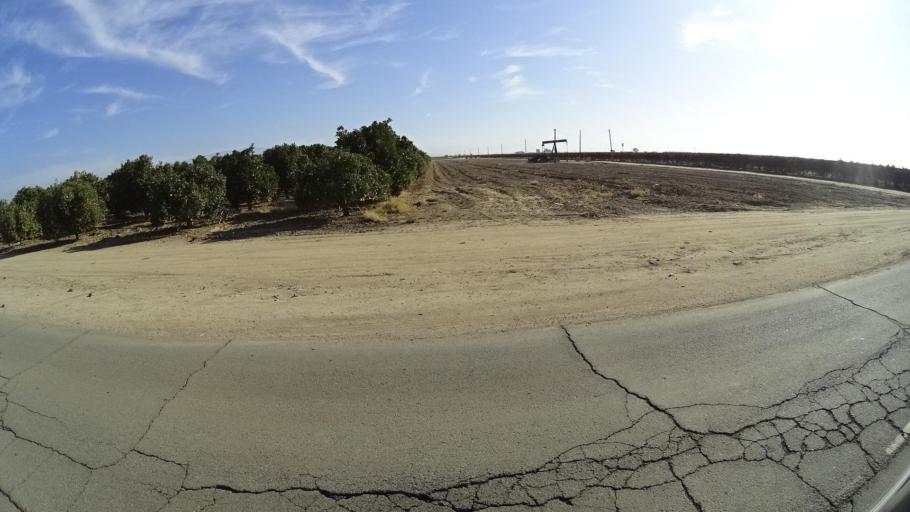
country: US
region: California
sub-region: Kern County
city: Lamont
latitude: 35.3427
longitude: -118.8966
